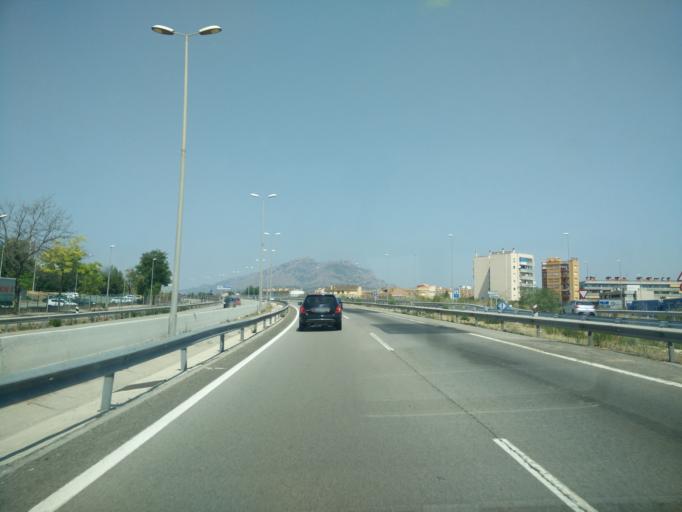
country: ES
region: Catalonia
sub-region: Provincia de Barcelona
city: Abrera
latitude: 41.5188
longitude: 1.8966
